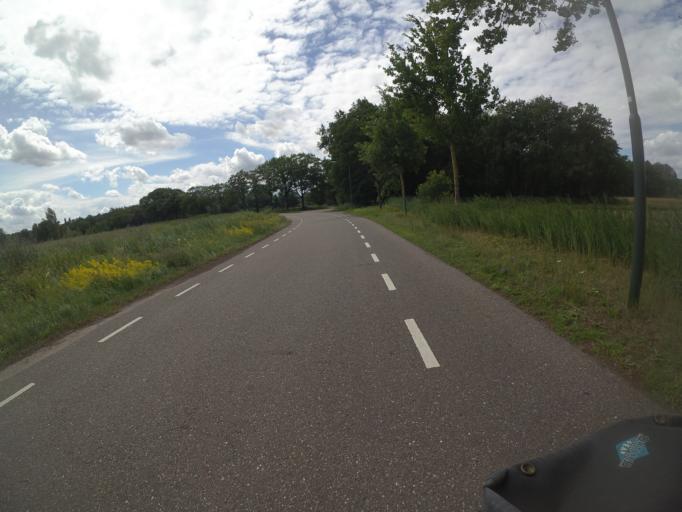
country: NL
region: North Brabant
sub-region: Gemeente Haaren
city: Haaren
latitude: 51.5894
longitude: 5.2434
